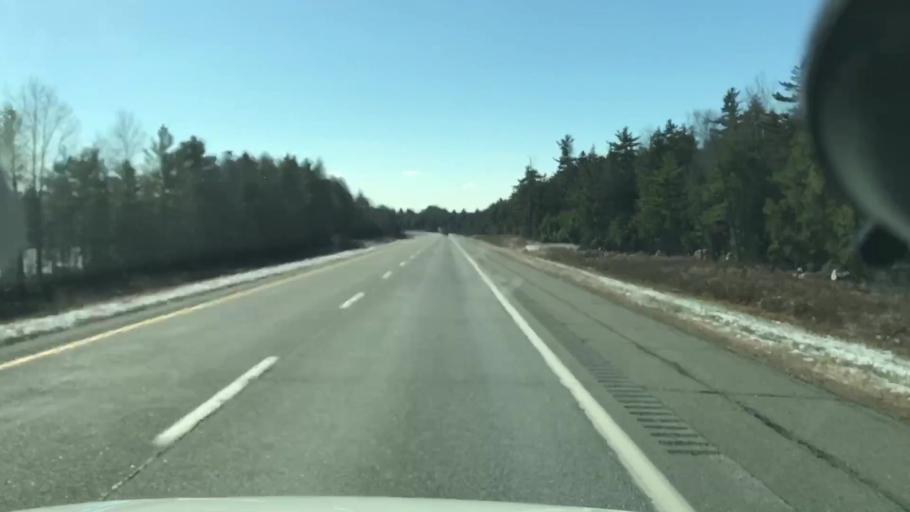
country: US
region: Maine
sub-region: Penobscot County
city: Howland
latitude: 45.2776
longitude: -68.6744
